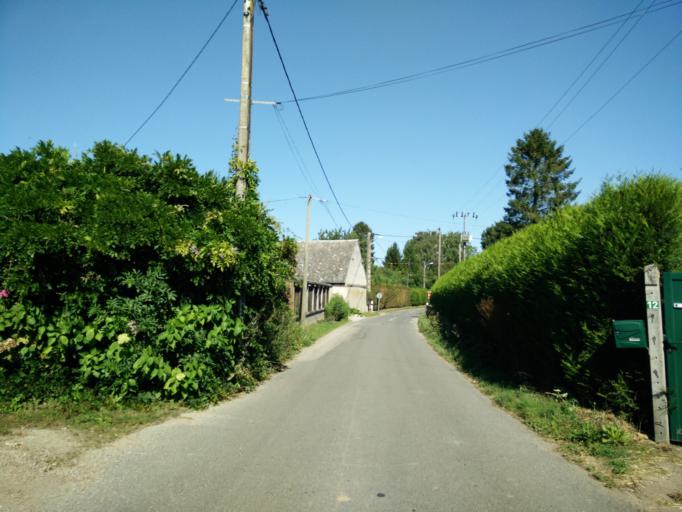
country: FR
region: Haute-Normandie
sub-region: Departement de l'Eure
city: La Haye-Malherbe
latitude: 49.1672
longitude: 1.0184
